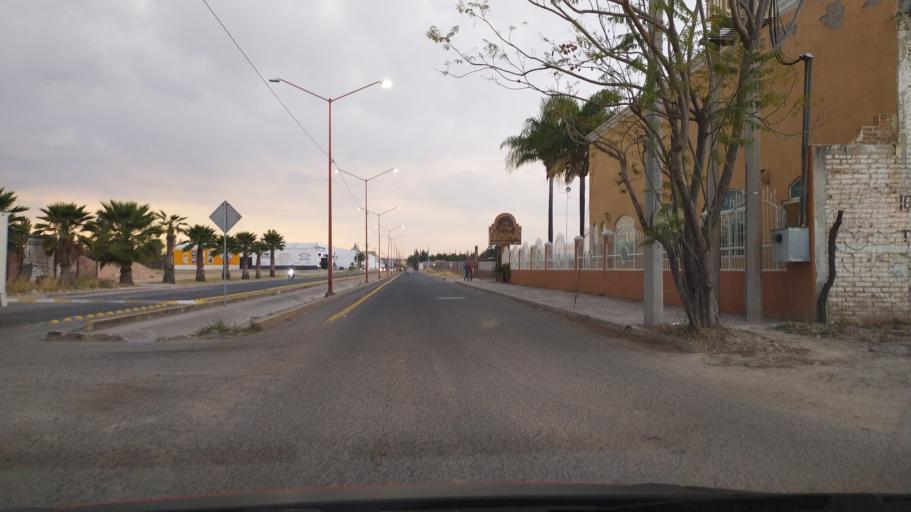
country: MX
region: Guanajuato
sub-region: Purisima del Rincon
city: Monte Grande
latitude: 21.0036
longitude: -101.8539
